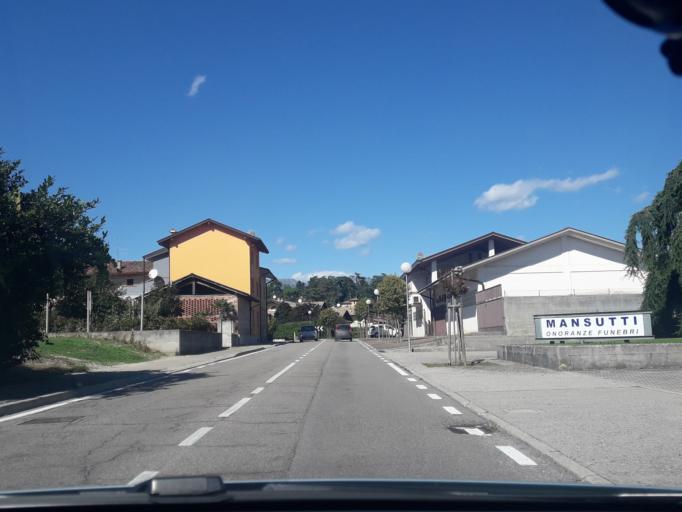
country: IT
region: Friuli Venezia Giulia
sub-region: Provincia di Udine
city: Tricesimo
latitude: 46.1559
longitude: 13.2156
